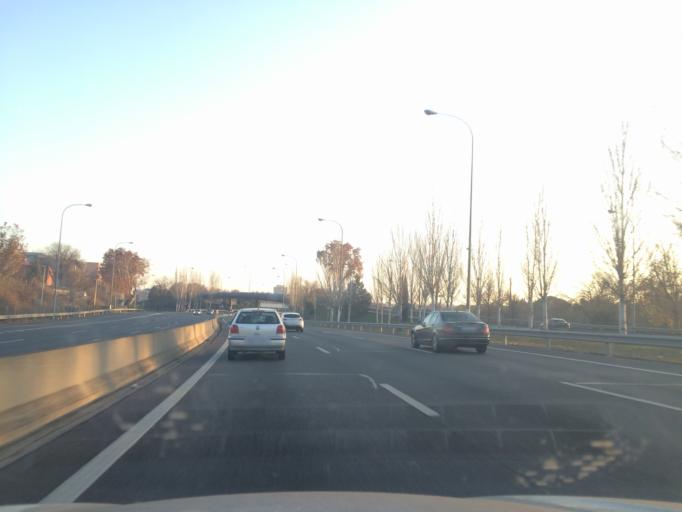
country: ES
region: Madrid
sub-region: Provincia de Madrid
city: Moncloa-Aravaca
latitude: 40.4402
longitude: -3.7389
